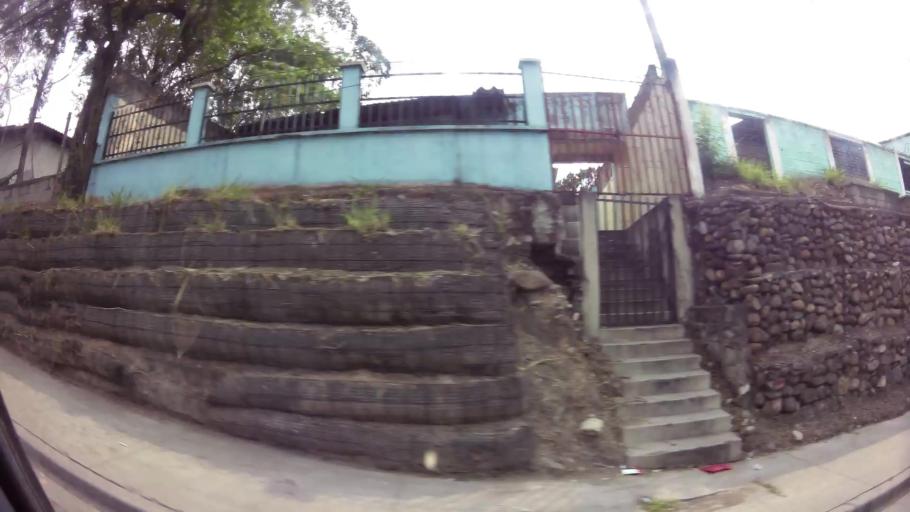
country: HN
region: Francisco Morazan
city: El Tablon
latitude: 14.0545
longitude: -87.1809
